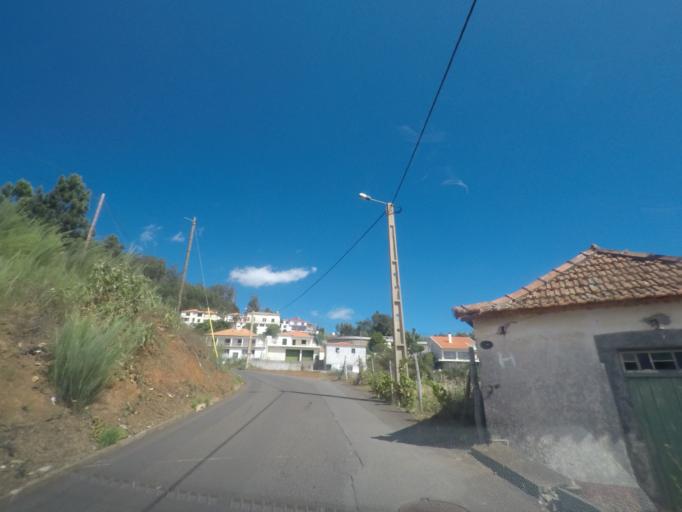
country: PT
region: Madeira
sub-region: Ribeira Brava
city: Campanario
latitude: 32.6800
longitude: -17.0421
